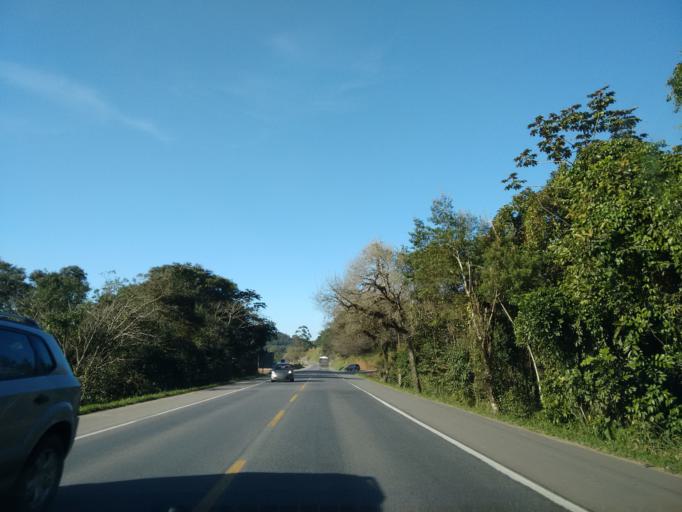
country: BR
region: Santa Catarina
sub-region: Joinville
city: Joinville
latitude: -26.4434
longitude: -48.8139
